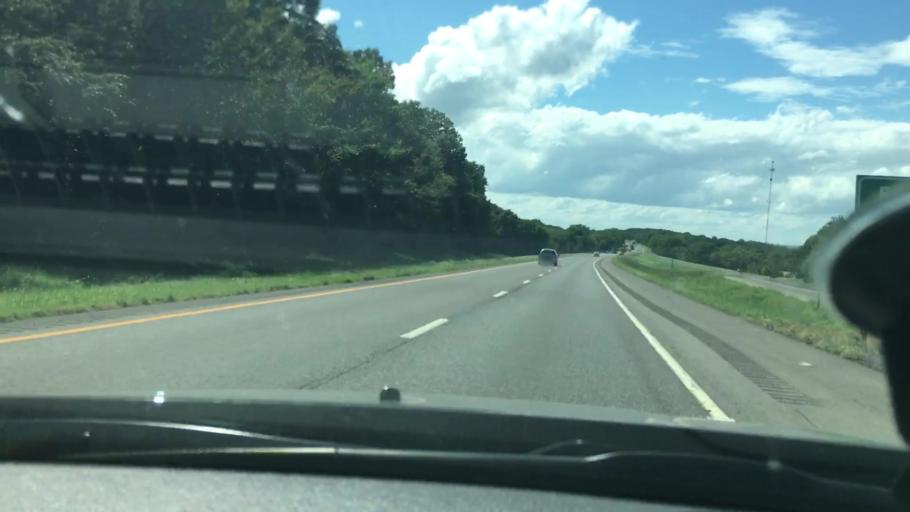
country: US
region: Oklahoma
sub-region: Sequoyah County
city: Vian
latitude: 35.4902
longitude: -95.0740
